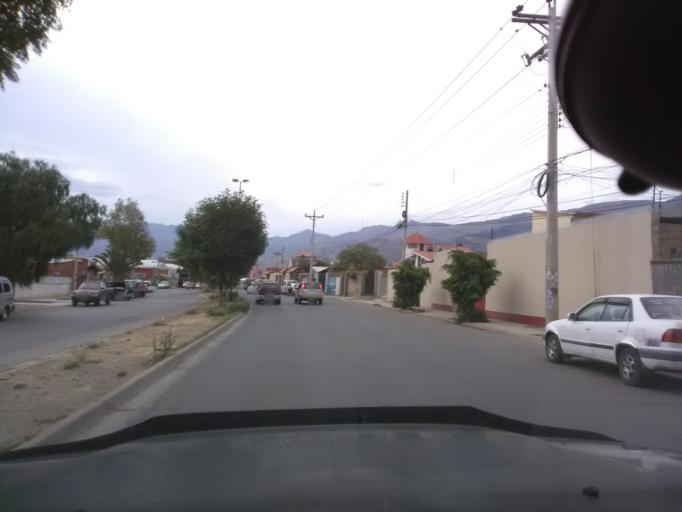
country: BO
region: Cochabamba
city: Cochabamba
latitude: -17.3553
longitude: -66.1786
